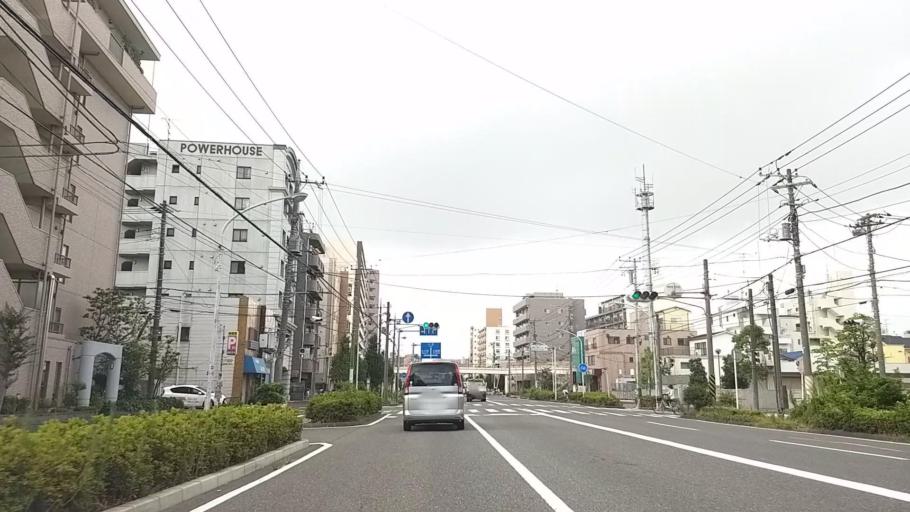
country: JP
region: Kanagawa
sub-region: Kawasaki-shi
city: Kawasaki
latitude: 35.5265
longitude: 139.7136
